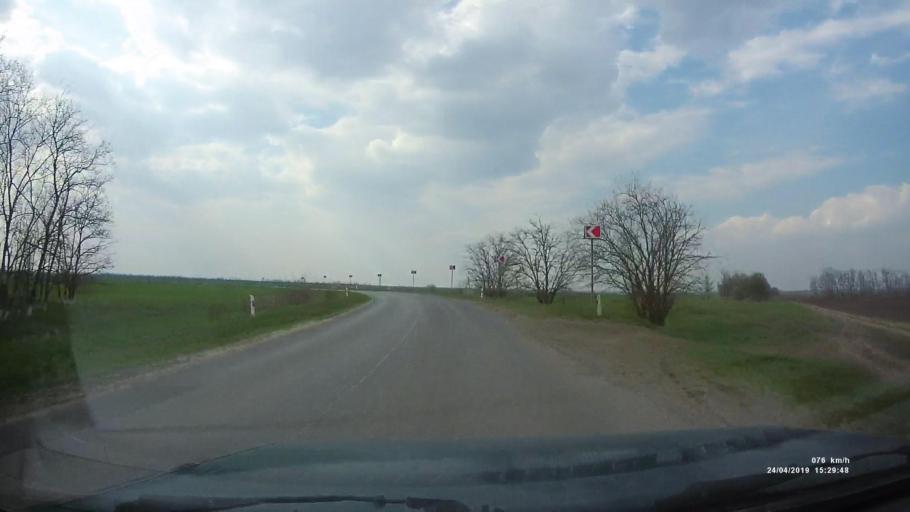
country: RU
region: Rostov
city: Remontnoye
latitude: 46.5987
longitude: 43.0172
